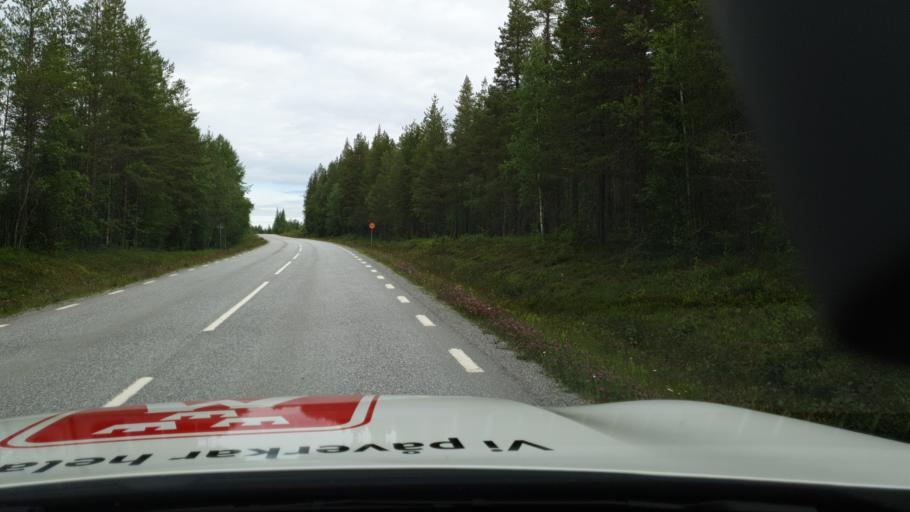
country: SE
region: Vaesterbotten
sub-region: Storumans Kommun
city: Storuman
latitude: 65.1642
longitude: 17.0383
